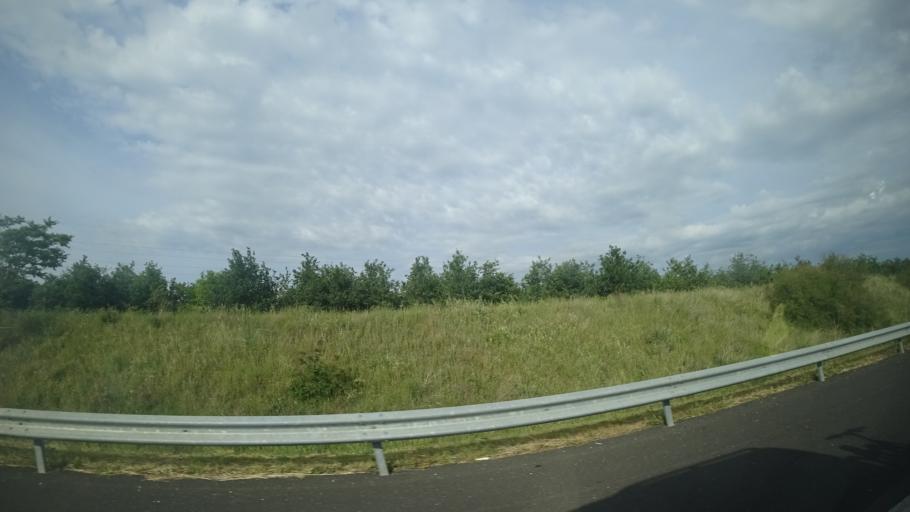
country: FR
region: Languedoc-Roussillon
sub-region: Departement de l'Herault
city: Nebian
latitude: 43.5997
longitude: 3.4623
